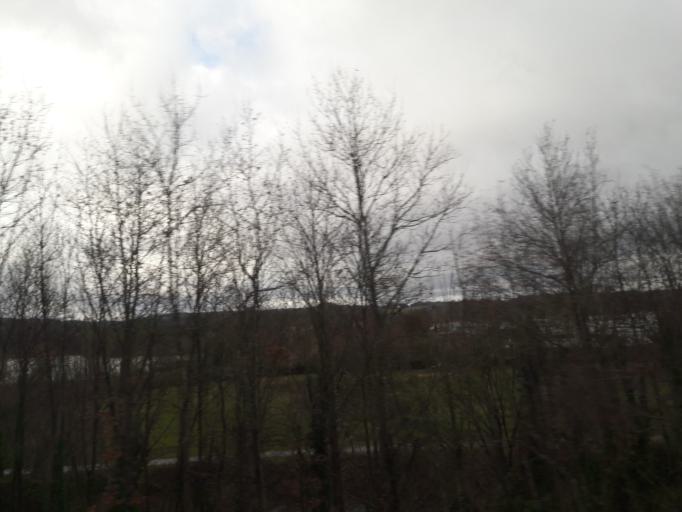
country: FR
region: Franche-Comte
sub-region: Territoire de Belfort
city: Andelnans
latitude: 47.5970
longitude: 6.8668
